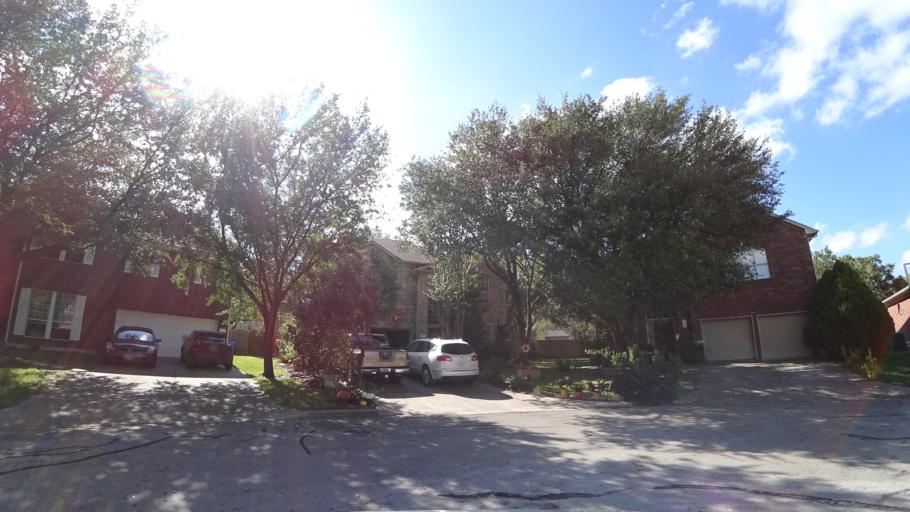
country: US
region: Texas
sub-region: Travis County
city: Windemere
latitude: 30.4574
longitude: -97.6568
